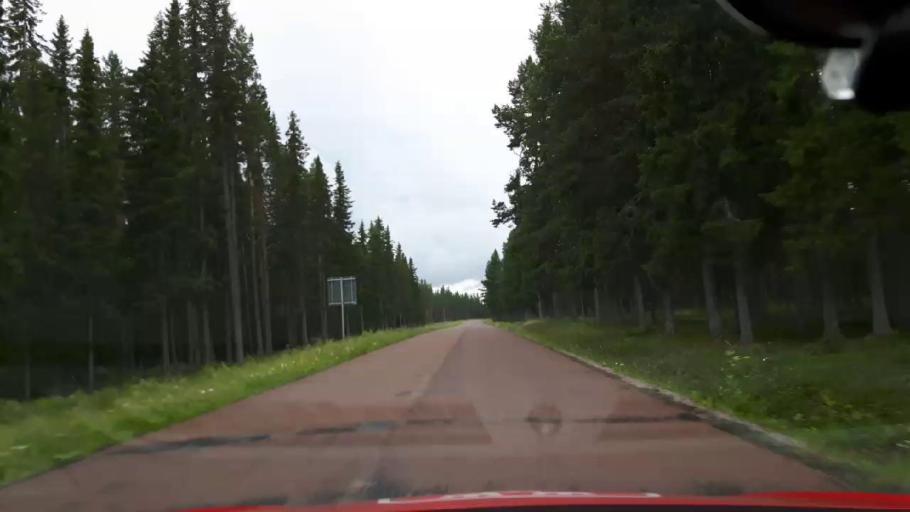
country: SE
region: Jaemtland
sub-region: Krokoms Kommun
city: Valla
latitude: 63.3582
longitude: 13.7302
